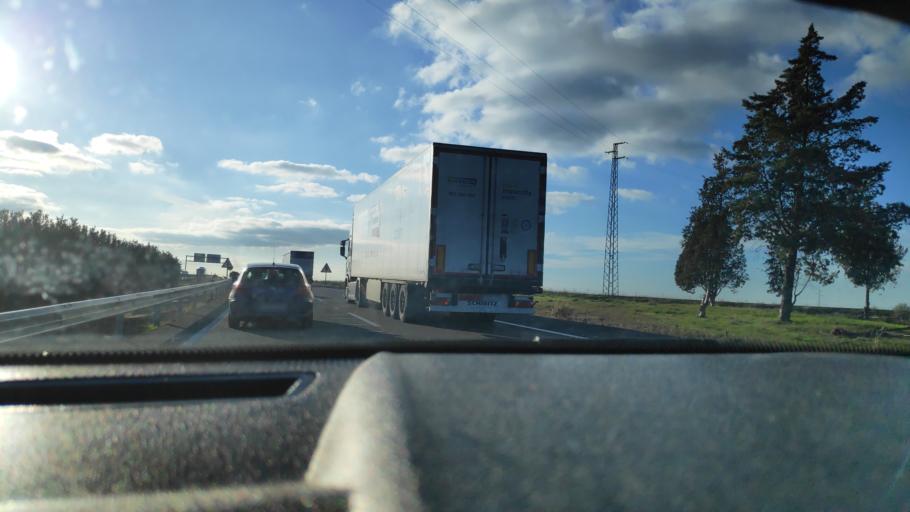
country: ES
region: Andalusia
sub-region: Provincia de Sevilla
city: Carmona
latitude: 37.4718
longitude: -5.6878
